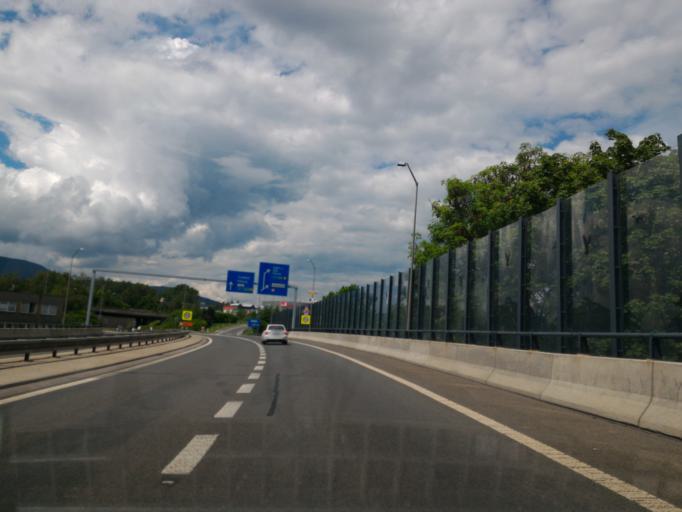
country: CZ
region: Liberecky
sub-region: Okres Liberec
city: Liberec
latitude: 50.7502
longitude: 15.0566
